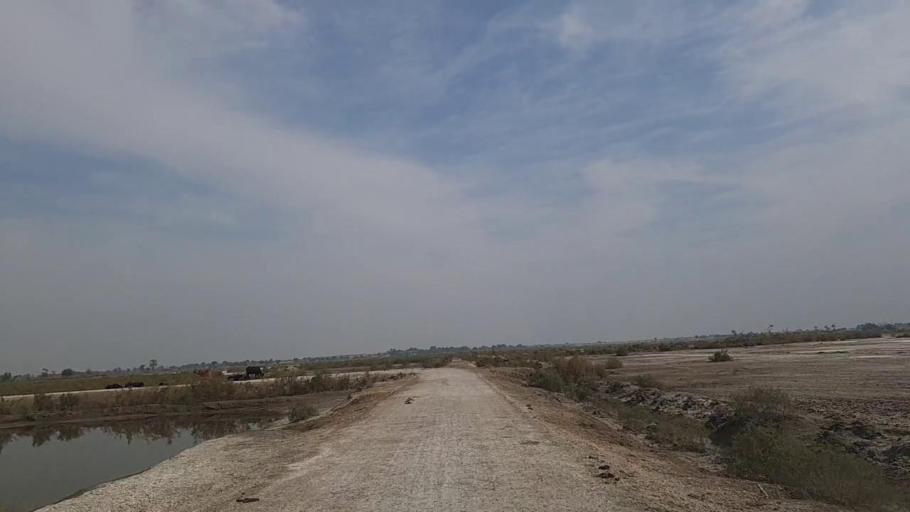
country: PK
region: Sindh
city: Daur
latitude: 26.4784
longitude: 68.4048
